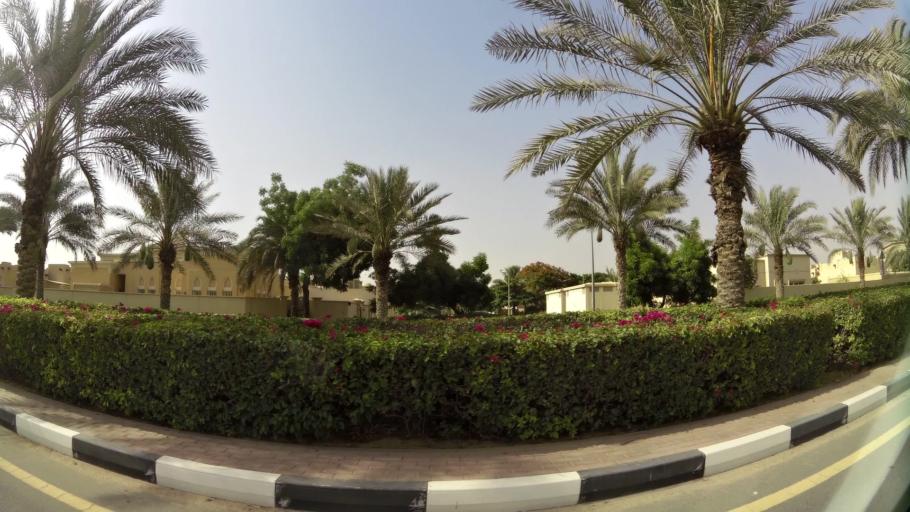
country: AE
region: Ash Shariqah
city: Sharjah
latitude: 25.2640
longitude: 55.4554
